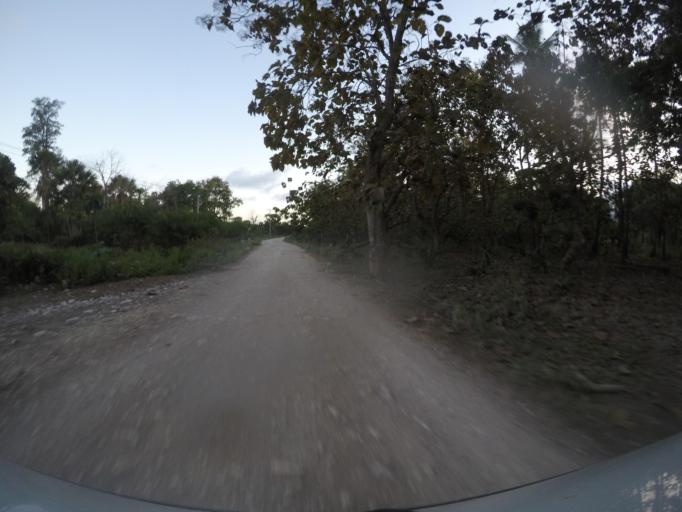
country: TL
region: Viqueque
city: Viqueque
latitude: -8.7687
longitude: 126.6433
